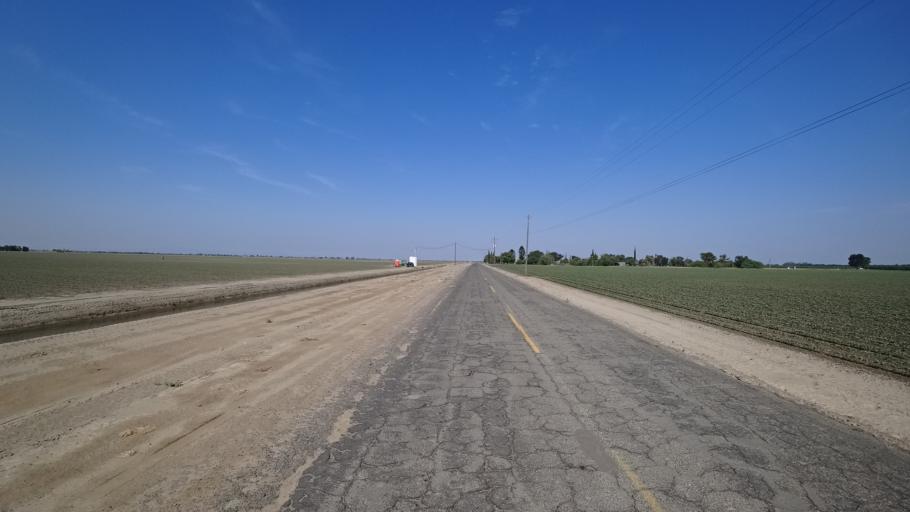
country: US
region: California
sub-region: Kings County
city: Lemoore
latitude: 36.3206
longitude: -119.8311
